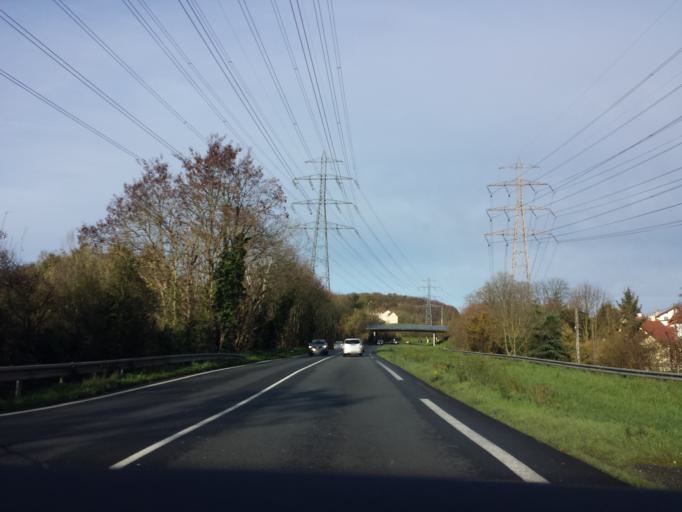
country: FR
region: Ile-de-France
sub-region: Departement de l'Essonne
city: Igny
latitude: 48.7360
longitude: 2.2291
